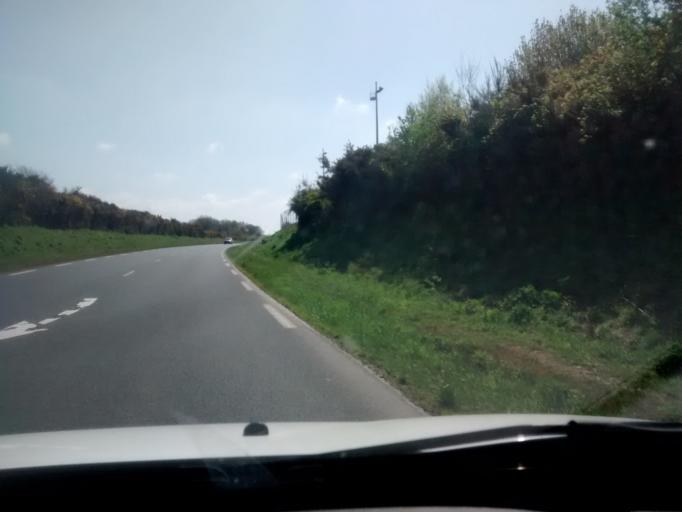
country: FR
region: Brittany
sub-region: Departement des Cotes-d'Armor
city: Saint-Quay-Perros
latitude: 48.7609
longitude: -3.4471
